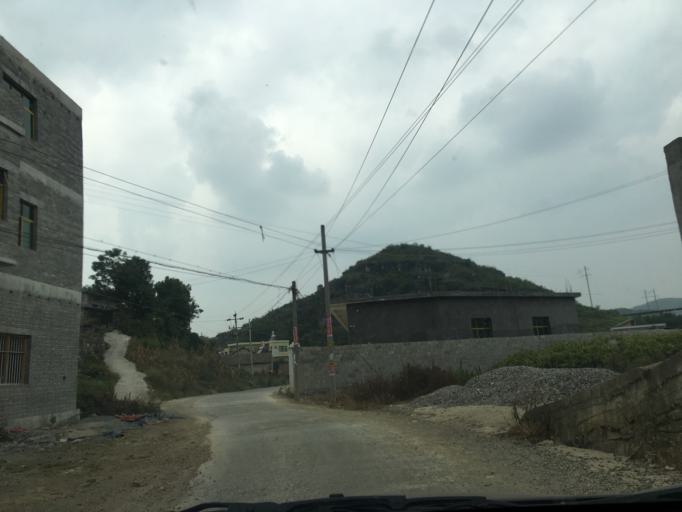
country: CN
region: Guangxi Zhuangzu Zizhiqu
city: Xinzhou
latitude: 25.5285
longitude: 105.6338
